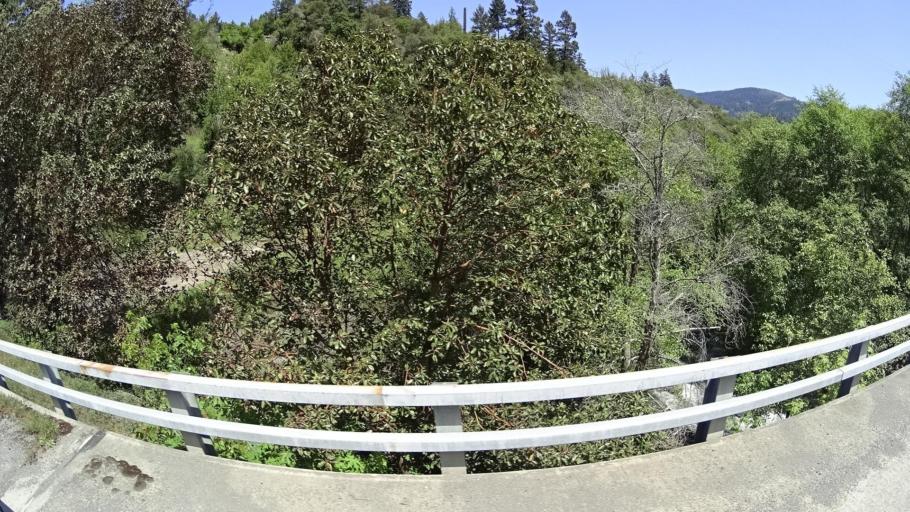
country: US
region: California
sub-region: Humboldt County
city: Redway
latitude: 40.2219
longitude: -123.6026
